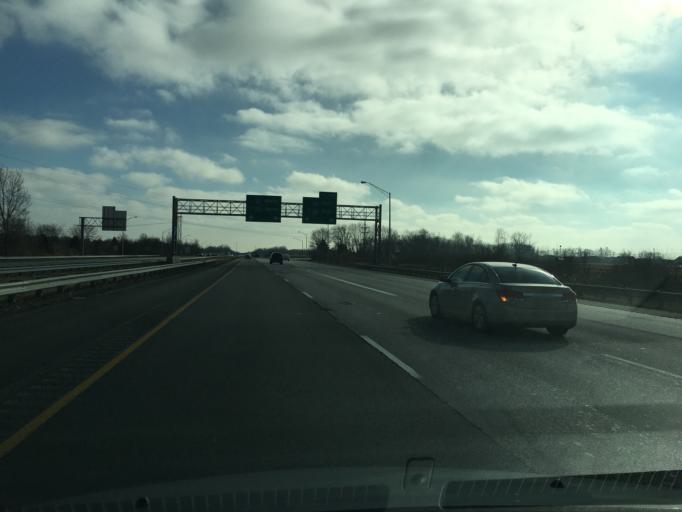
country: US
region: Indiana
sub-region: Boone County
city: Whitestown
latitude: 39.9393
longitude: -86.3463
